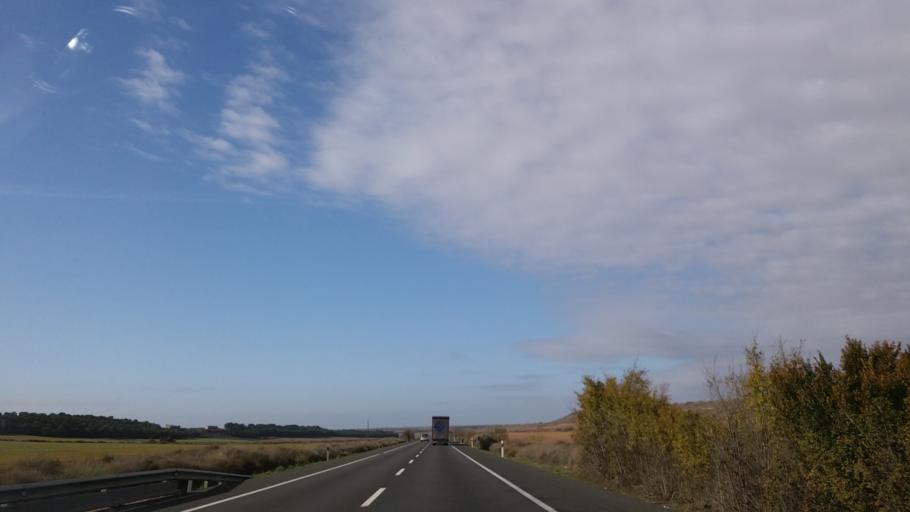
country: ES
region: Aragon
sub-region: Provincia de Huesca
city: Ballobar
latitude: 41.5204
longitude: 0.1863
